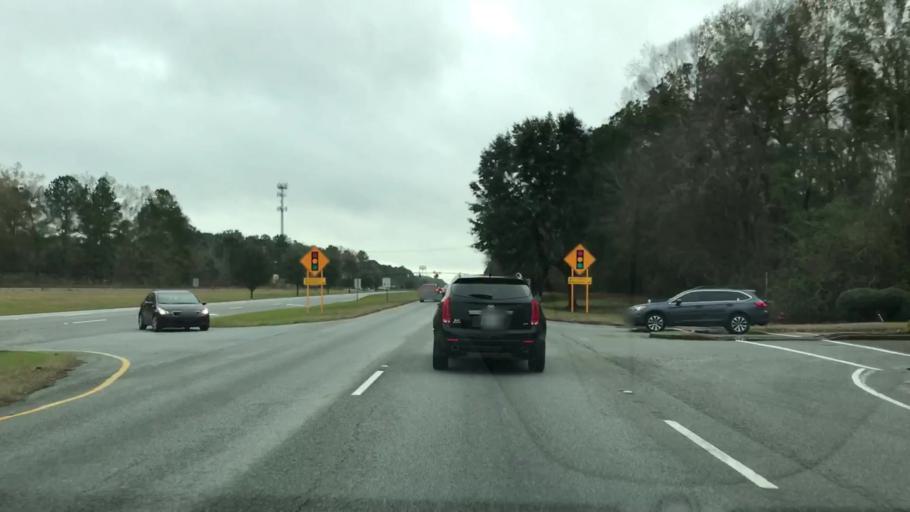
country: US
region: South Carolina
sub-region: Berkeley County
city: Goose Creek
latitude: 33.0209
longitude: -80.0359
